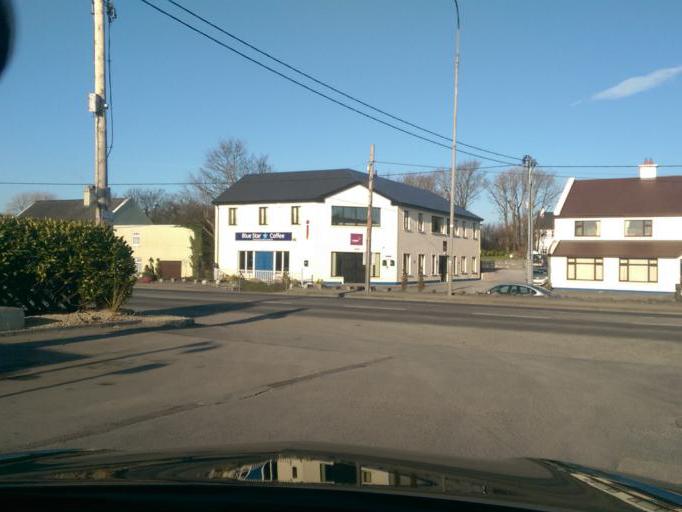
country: IE
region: Connaught
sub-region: County Galway
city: Oranmore
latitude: 53.2089
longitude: -8.8687
